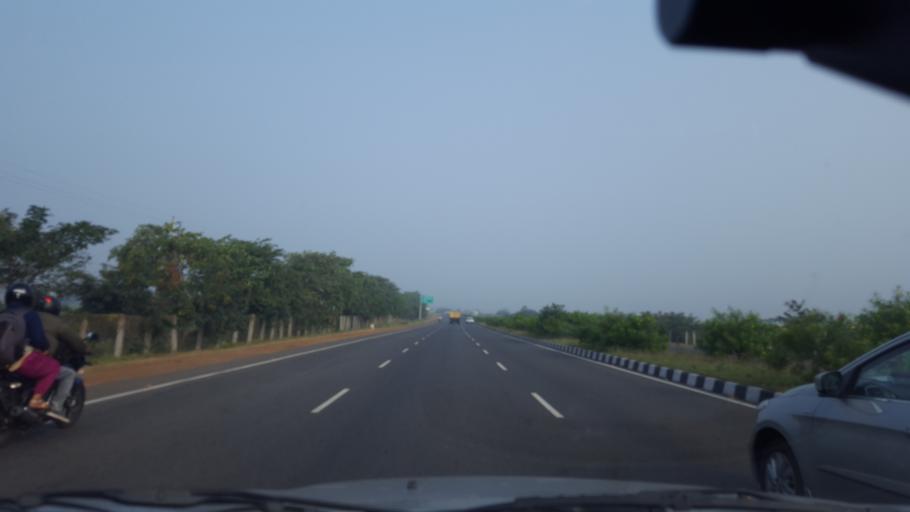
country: IN
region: Andhra Pradesh
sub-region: Prakasam
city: Ongole
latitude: 15.3825
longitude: 80.0406
